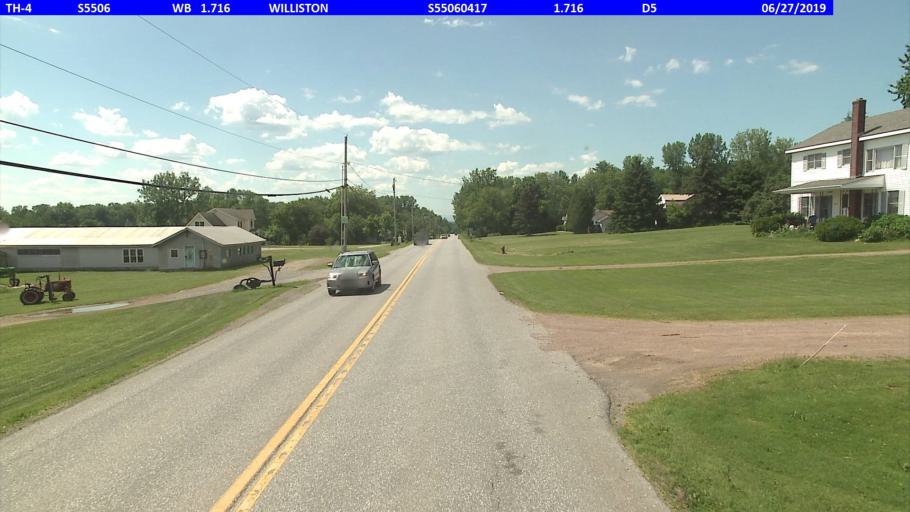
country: US
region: Vermont
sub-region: Chittenden County
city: Williston
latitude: 44.4575
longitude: -73.0820
